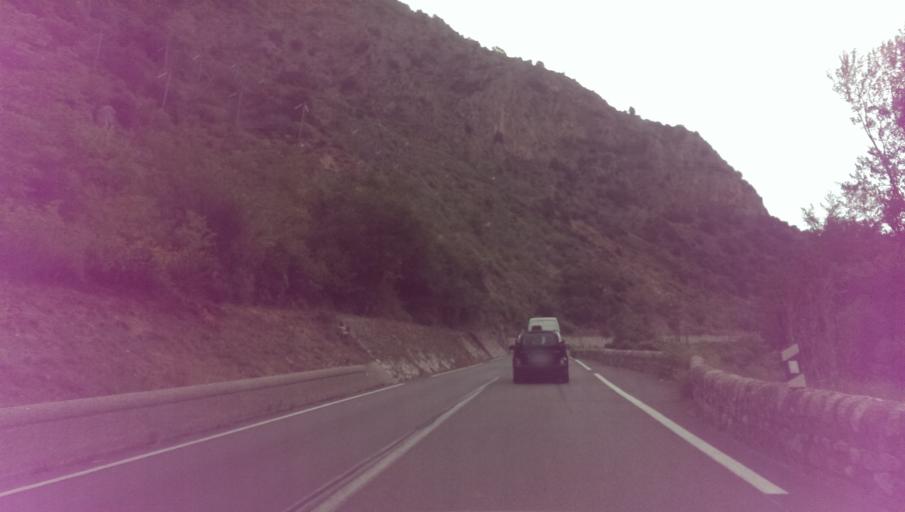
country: FR
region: Languedoc-Roussillon
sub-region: Departement des Pyrenees-Orientales
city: Vernet-les-Bains
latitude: 42.5826
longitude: 2.3539
